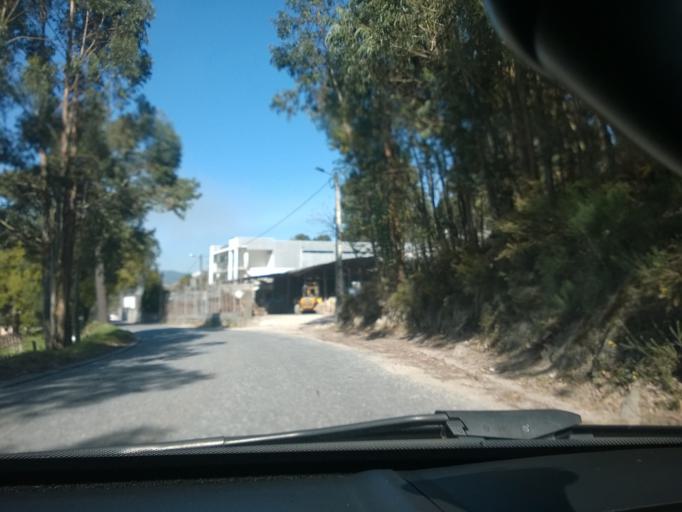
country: PT
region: Aveiro
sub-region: Castelo de Paiva
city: Castelo de Paiva
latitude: 41.1220
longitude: -8.2795
